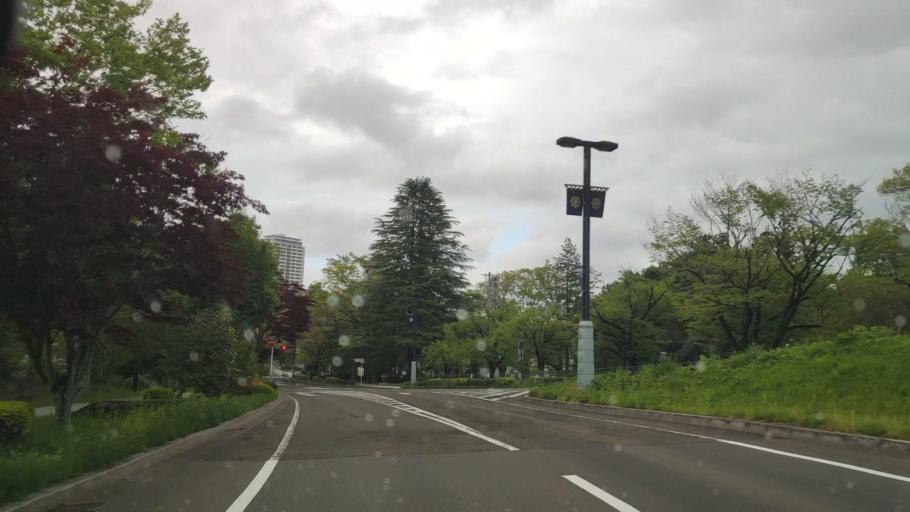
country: JP
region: Miyagi
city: Sendai
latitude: 38.2576
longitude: 140.8562
